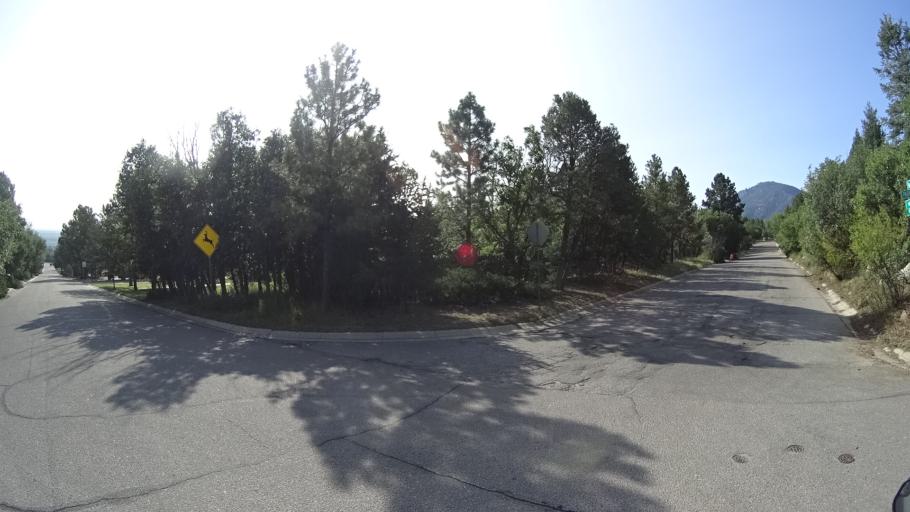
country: US
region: Colorado
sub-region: El Paso County
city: Colorado Springs
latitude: 38.8119
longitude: -104.8650
